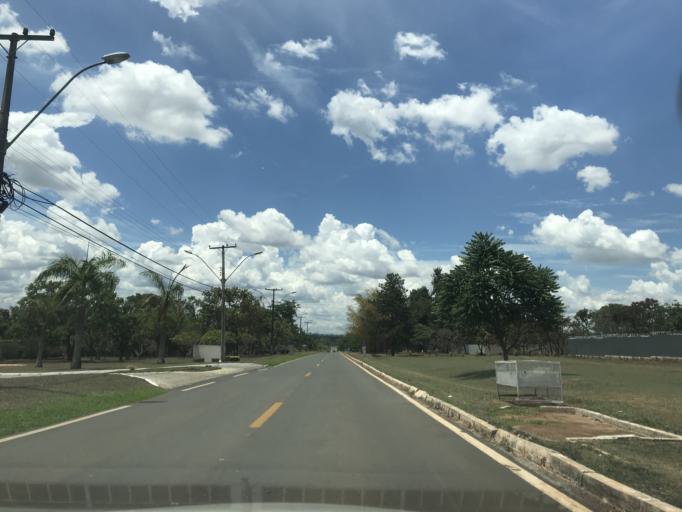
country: BR
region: Federal District
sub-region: Brasilia
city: Brasilia
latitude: -15.9060
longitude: -47.9456
